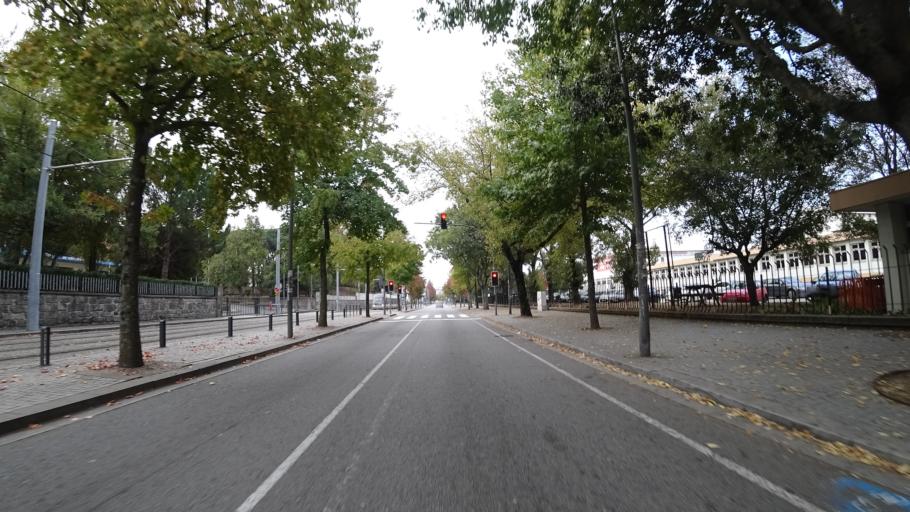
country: PT
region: Porto
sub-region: Matosinhos
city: Sao Mamede de Infesta
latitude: 41.1826
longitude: -8.6040
